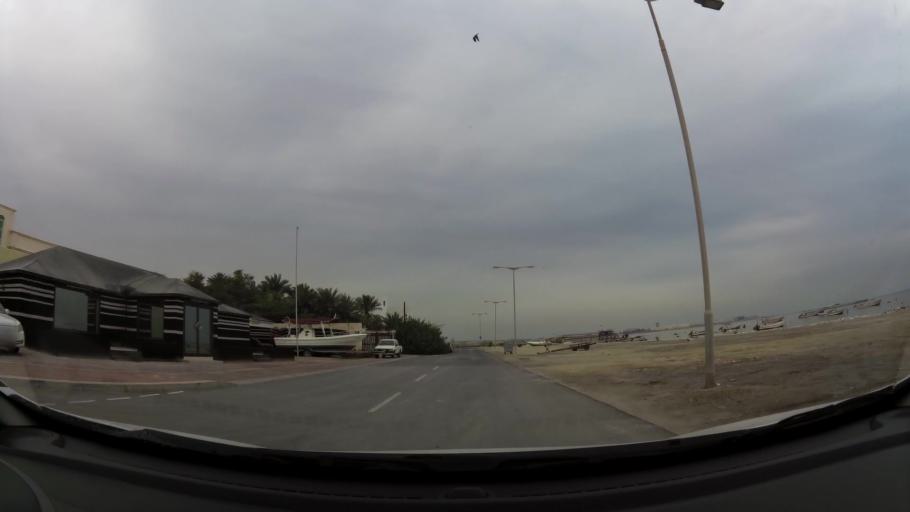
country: BH
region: Northern
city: Ar Rifa'
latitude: 26.0597
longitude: 50.6185
